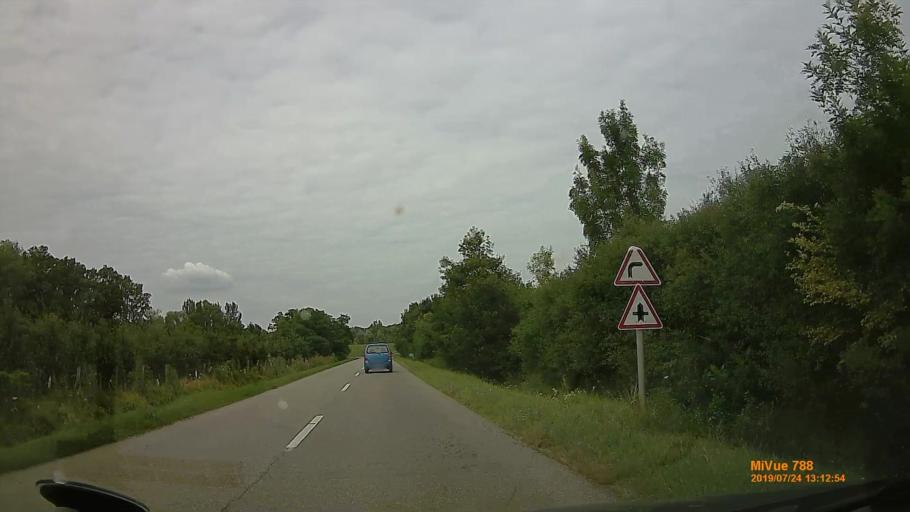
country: HU
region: Szabolcs-Szatmar-Bereg
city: Vasarosnameny
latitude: 48.1651
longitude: 22.3388
